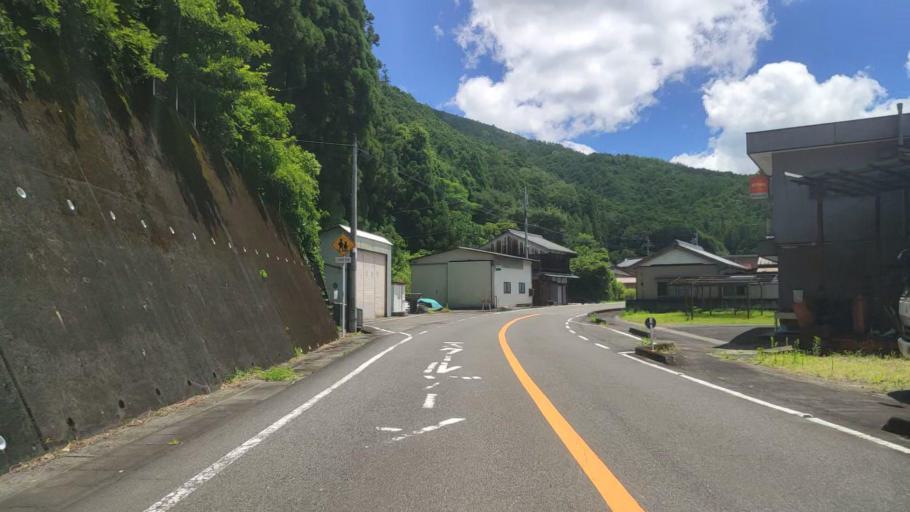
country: JP
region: Mie
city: Owase
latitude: 33.9863
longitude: 136.0474
